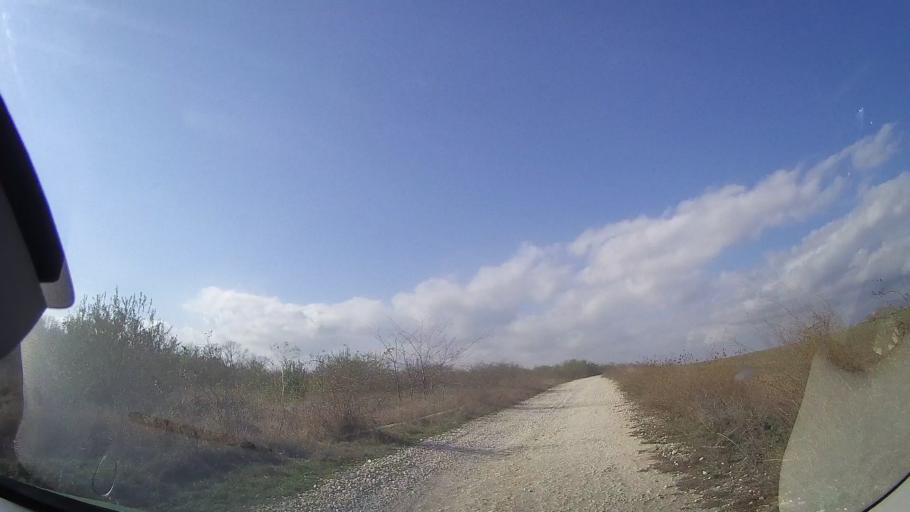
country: RO
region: Constanta
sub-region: Comuna Douazeci si Trei August
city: Douazeci si Trei August
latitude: 43.9045
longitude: 28.6181
